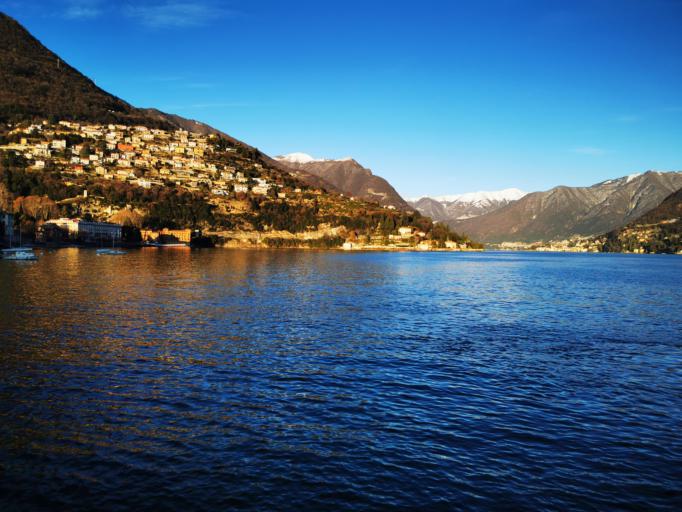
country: IT
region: Lombardy
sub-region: Provincia di Como
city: Cernobbio
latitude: 45.8392
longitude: 9.0787
